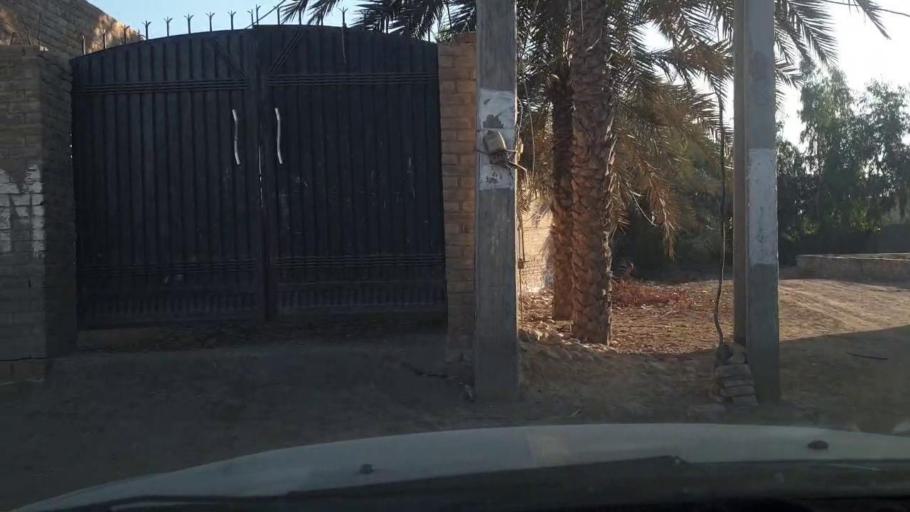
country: PK
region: Sindh
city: Ghotki
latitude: 28.0195
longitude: 69.3060
